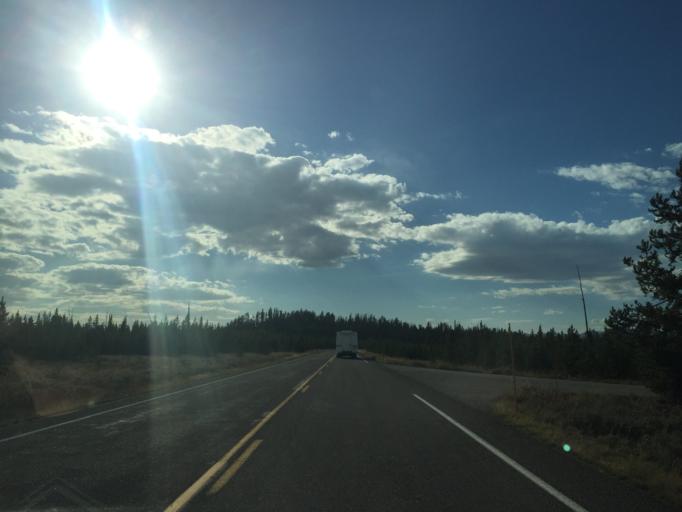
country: US
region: Montana
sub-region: Gallatin County
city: West Yellowstone
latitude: 44.6511
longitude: -111.0315
